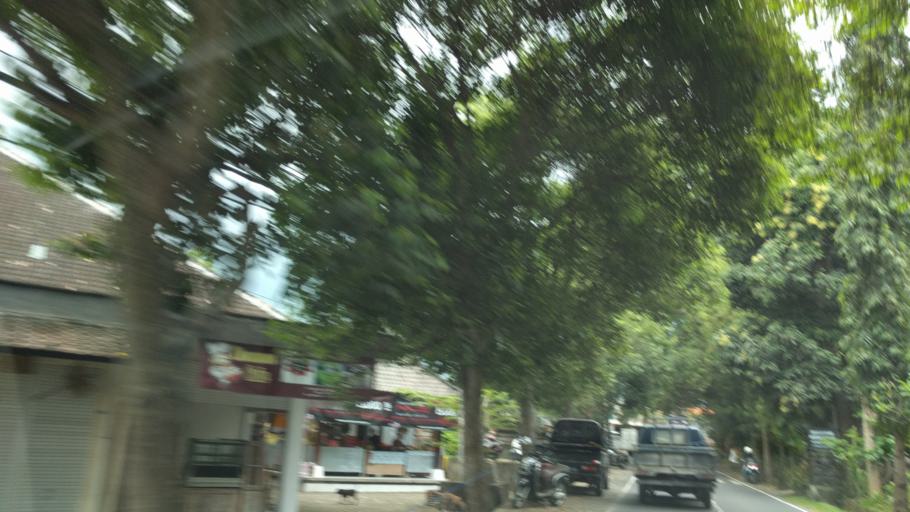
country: ID
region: Bali
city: Banjar Pande
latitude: -8.5195
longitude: 115.2401
